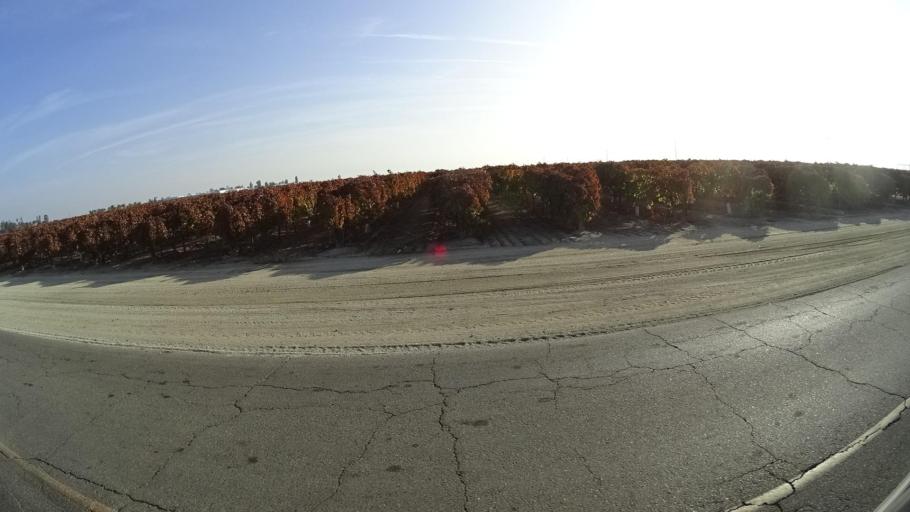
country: US
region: California
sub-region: Kern County
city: Delano
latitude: 35.7696
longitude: -119.1875
